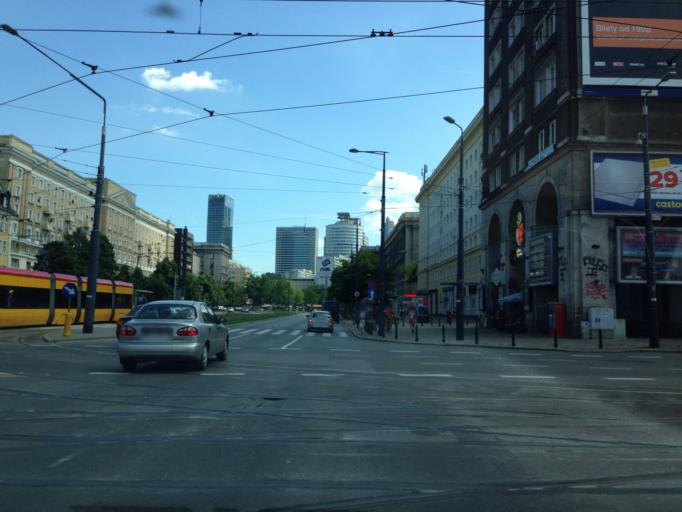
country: PL
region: Masovian Voivodeship
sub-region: Warszawa
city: Wola
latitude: 52.2419
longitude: 20.9934
